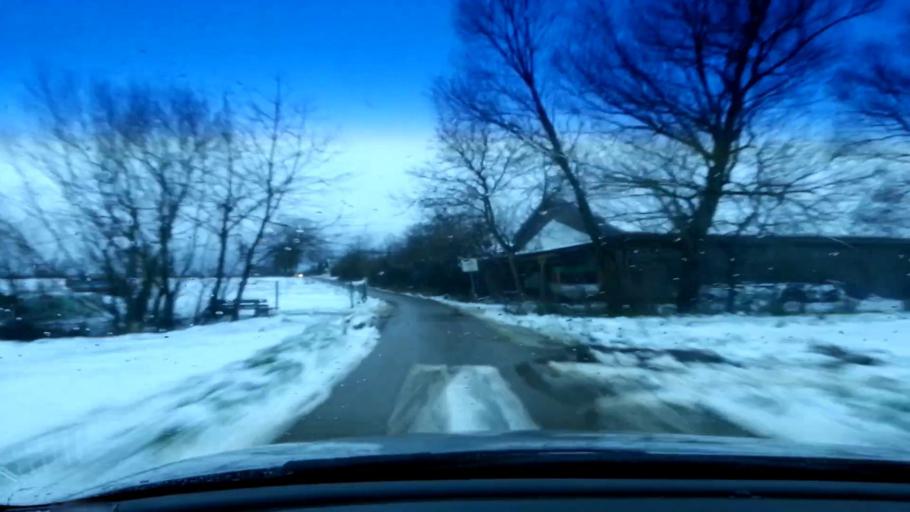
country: DE
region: Bavaria
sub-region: Upper Franconia
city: Litzendorf
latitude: 49.9539
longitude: 10.9970
